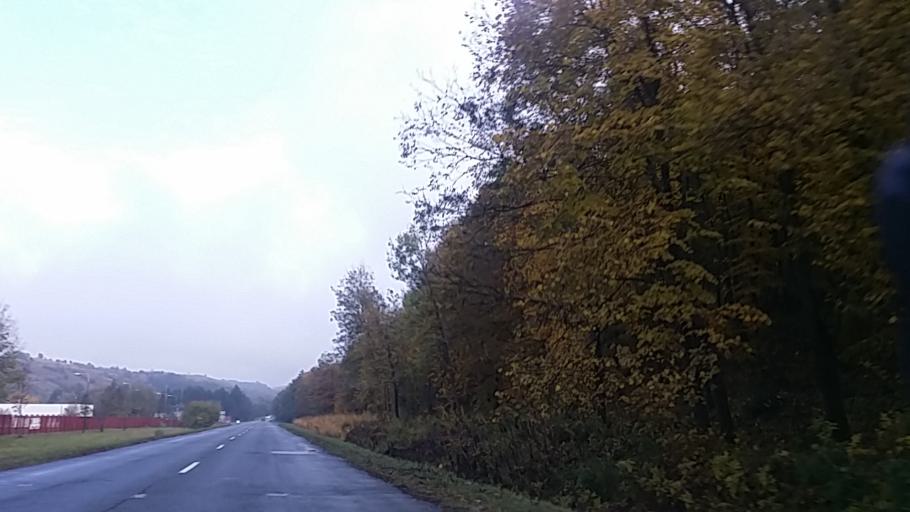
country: HU
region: Heves
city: Belapatfalva
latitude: 48.0695
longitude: 20.3570
